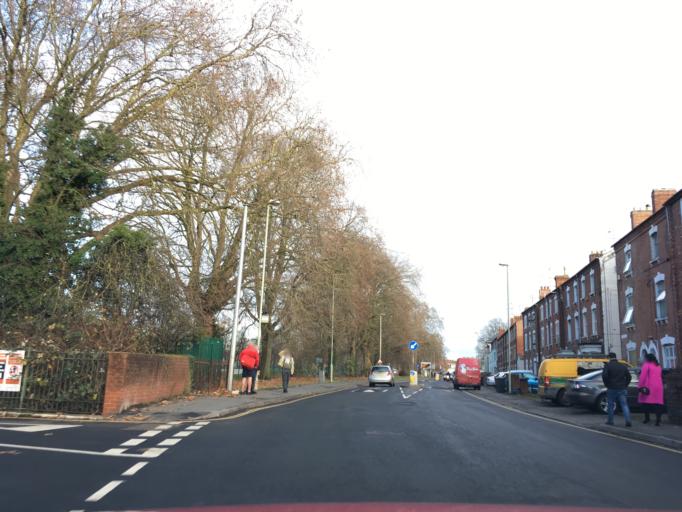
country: GB
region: England
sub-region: Gloucestershire
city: Gloucester
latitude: 51.8565
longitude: -2.2438
